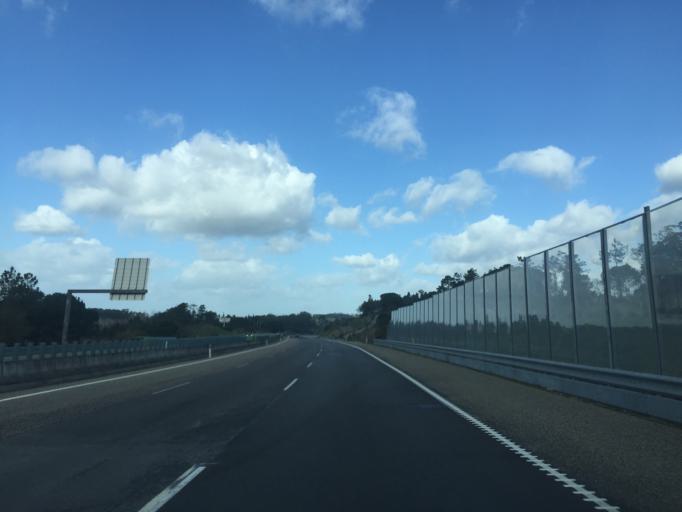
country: PT
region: Leiria
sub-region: Leiria
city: Souto da Carpalhosa
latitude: 39.8331
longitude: -8.8338
